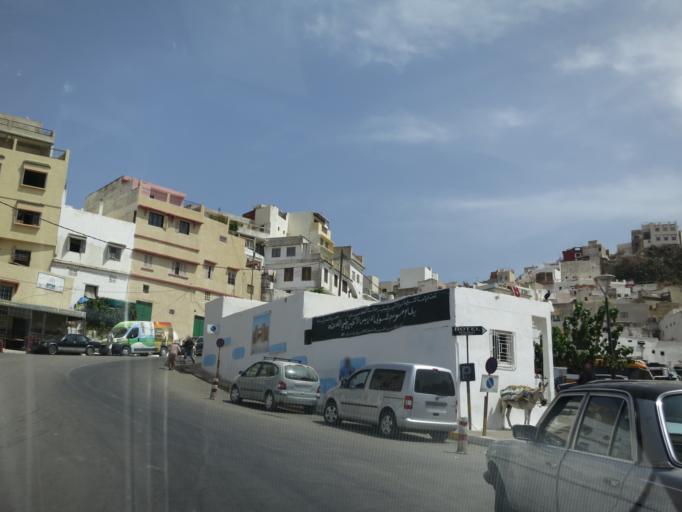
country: MA
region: Meknes-Tafilalet
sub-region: Meknes
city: Meknes
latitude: 34.0572
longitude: -5.5241
